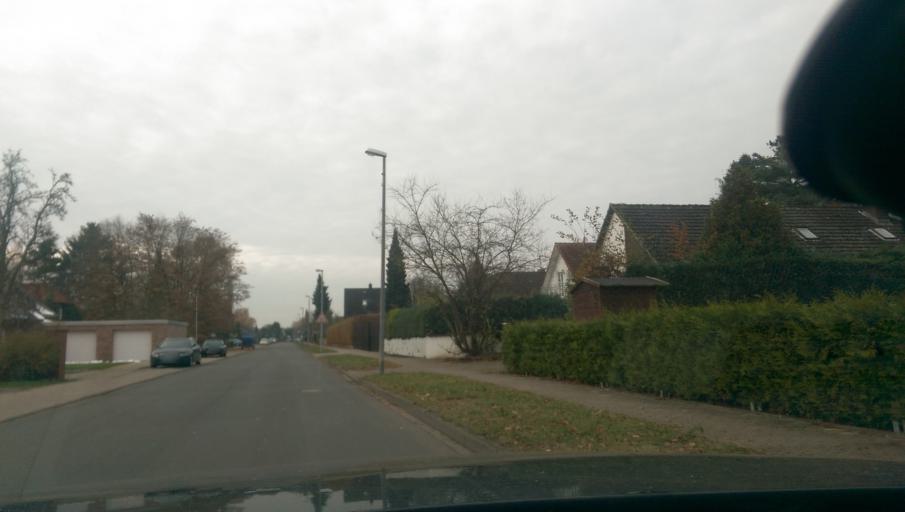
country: DE
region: Lower Saxony
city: Garbsen-Mitte
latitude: 52.5050
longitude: 9.6292
